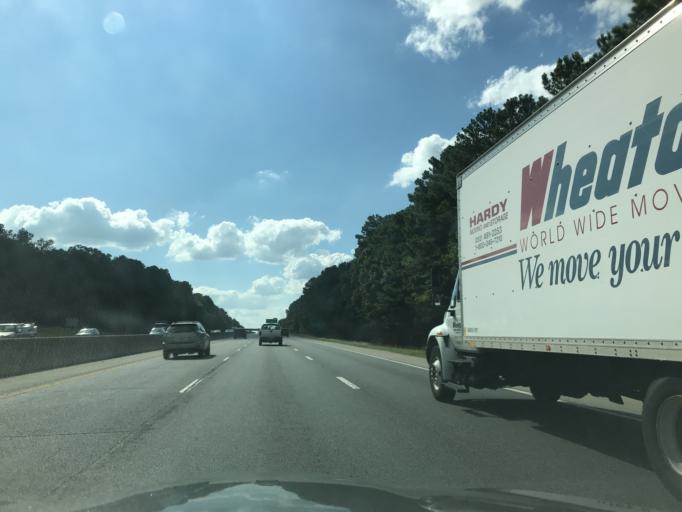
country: US
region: North Carolina
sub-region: Durham County
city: Durham
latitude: 35.9082
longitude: -78.9080
